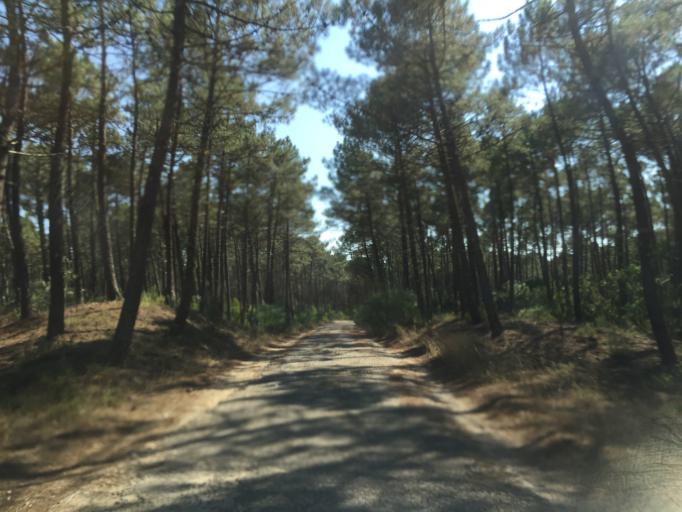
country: PT
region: Coimbra
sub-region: Figueira da Foz
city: Tavarede
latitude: 40.2494
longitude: -8.8423
